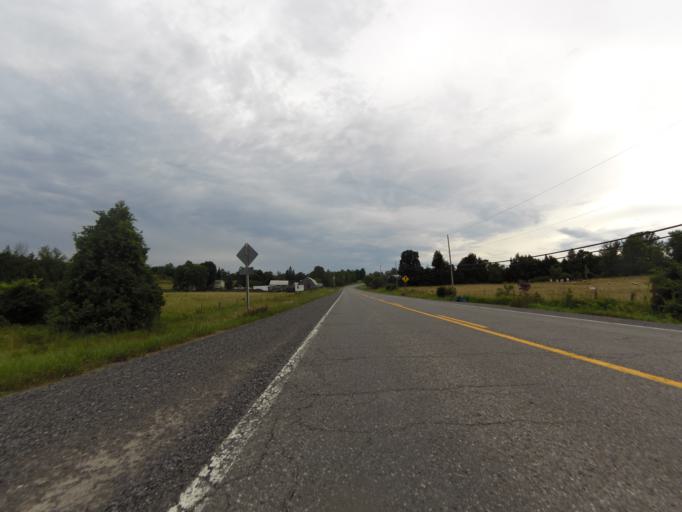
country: CA
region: Ontario
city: Carleton Place
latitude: 45.1593
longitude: -76.2956
